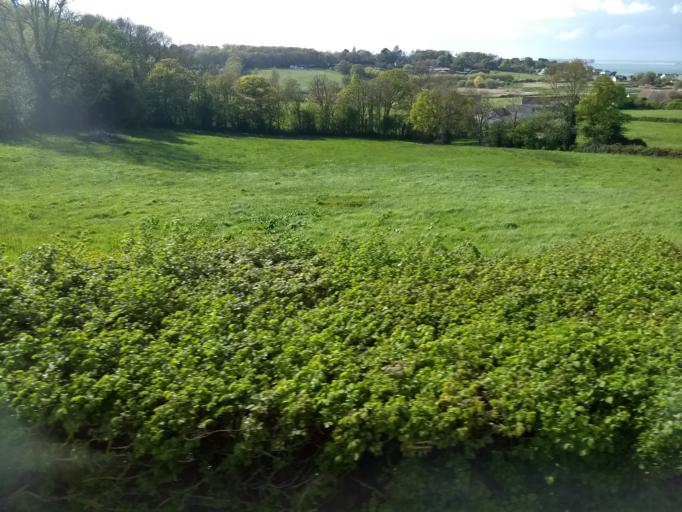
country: GB
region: England
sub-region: Isle of Wight
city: Seaview
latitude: 50.7167
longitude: -1.1149
